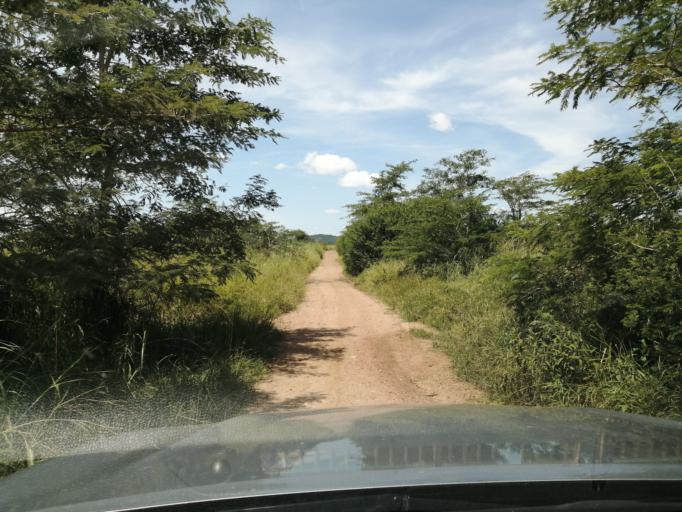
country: ZM
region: Central
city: Chibombo
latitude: -15.0658
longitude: 27.8322
